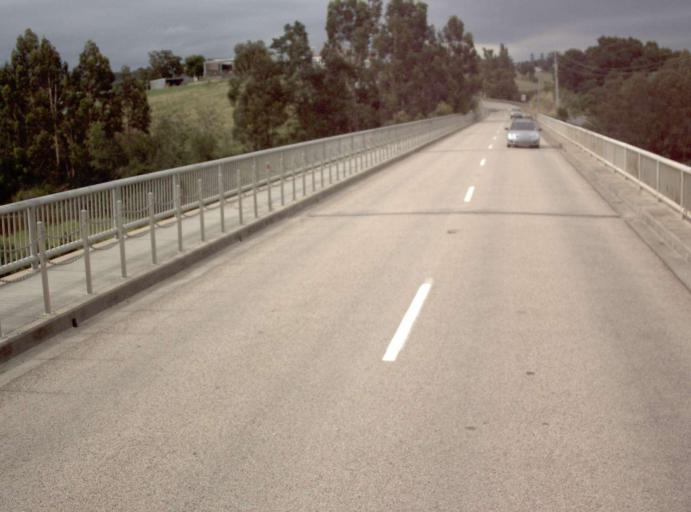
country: AU
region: Victoria
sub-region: East Gippsland
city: Lakes Entrance
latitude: -37.7115
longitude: 147.8359
